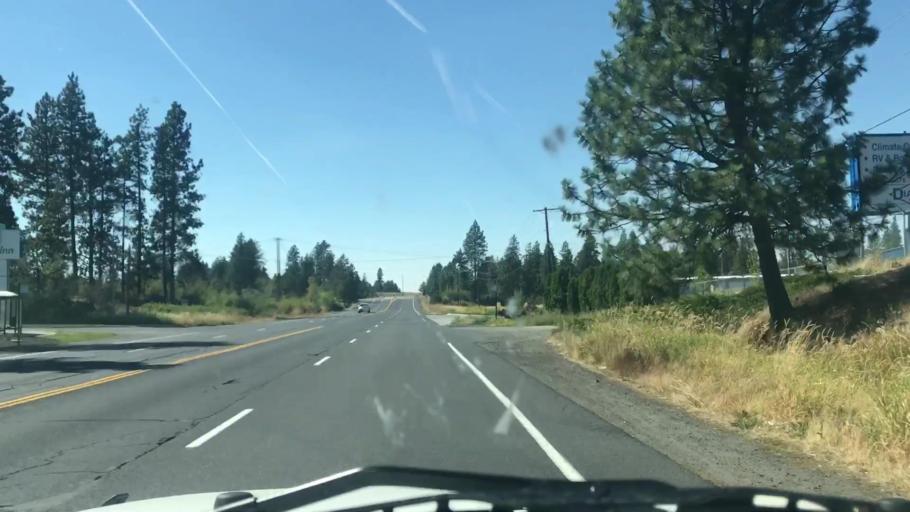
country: US
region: Washington
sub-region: Spokane County
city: Spokane
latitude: 47.6431
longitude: -117.4927
